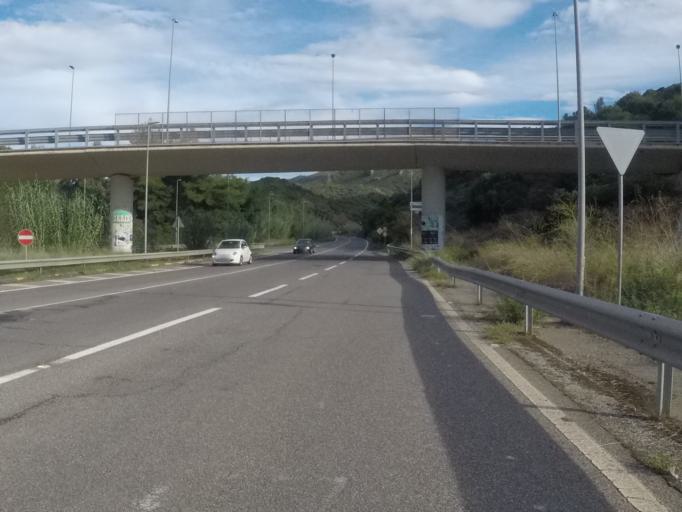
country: IT
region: Sardinia
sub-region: Provincia di Carbonia-Iglesias
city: Gonnesa
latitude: 39.2772
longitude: 8.4683
